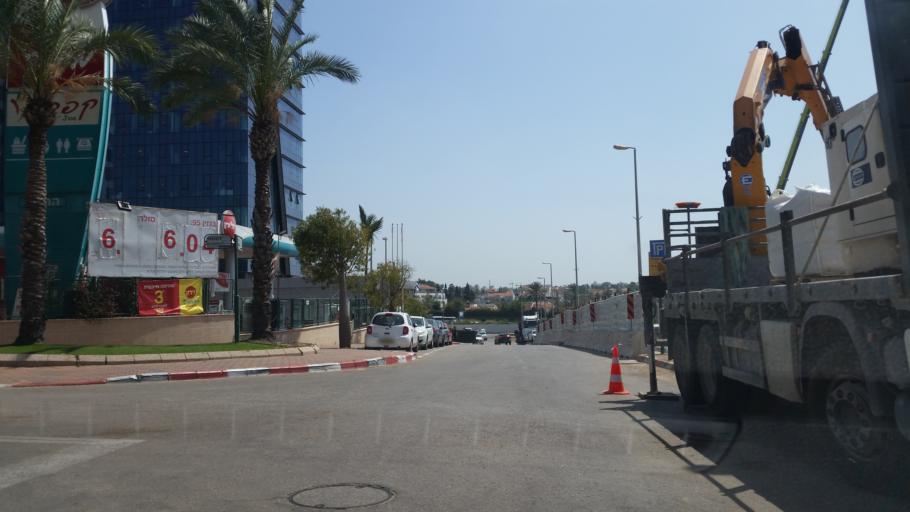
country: IL
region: Central District
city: Ra'anana
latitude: 32.1944
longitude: 34.8827
